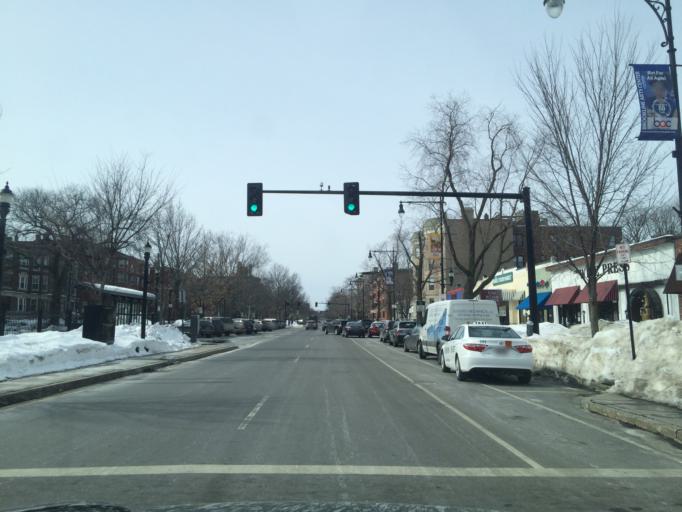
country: US
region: Massachusetts
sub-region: Norfolk County
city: Brookline
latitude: 42.3461
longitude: -71.1073
